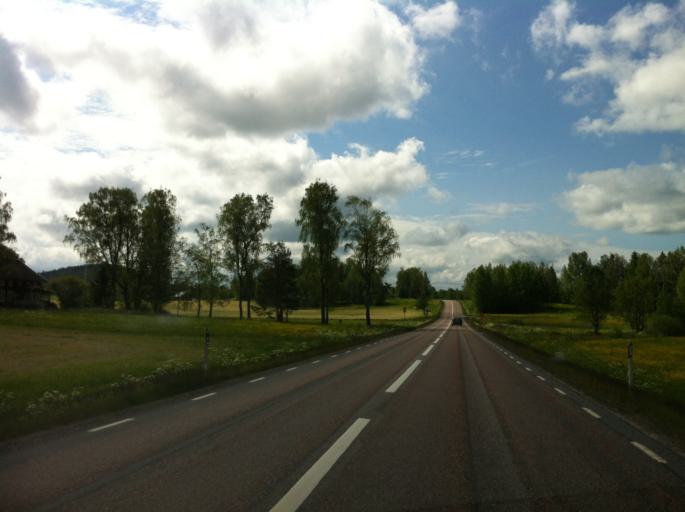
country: SE
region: Vaermland
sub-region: Sunne Kommun
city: Sunne
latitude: 59.6471
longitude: 13.1560
